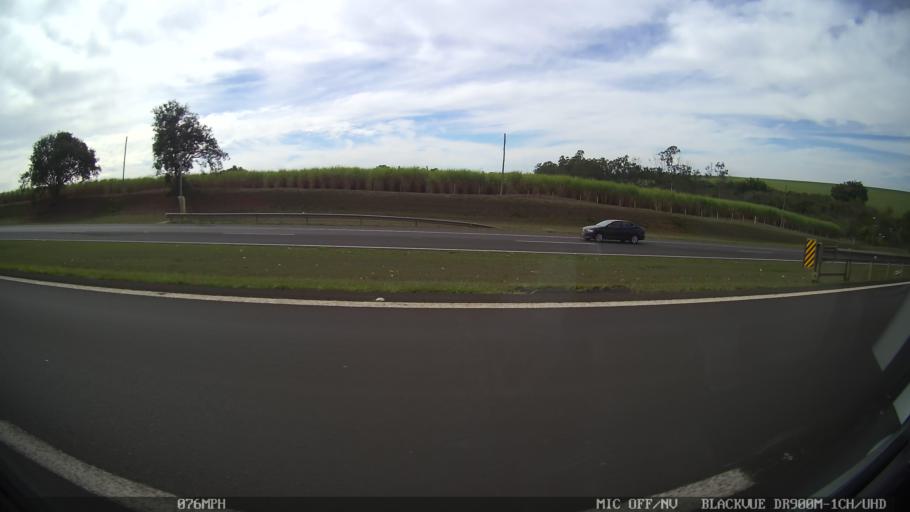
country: BR
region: Sao Paulo
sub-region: Matao
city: Matao
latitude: -21.5519
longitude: -48.4880
